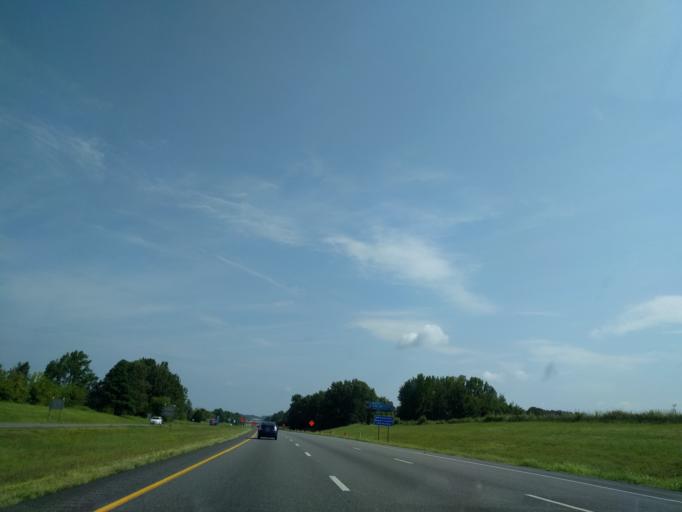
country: US
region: Tennessee
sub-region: Sumner County
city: Portland
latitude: 36.6115
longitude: -86.5797
